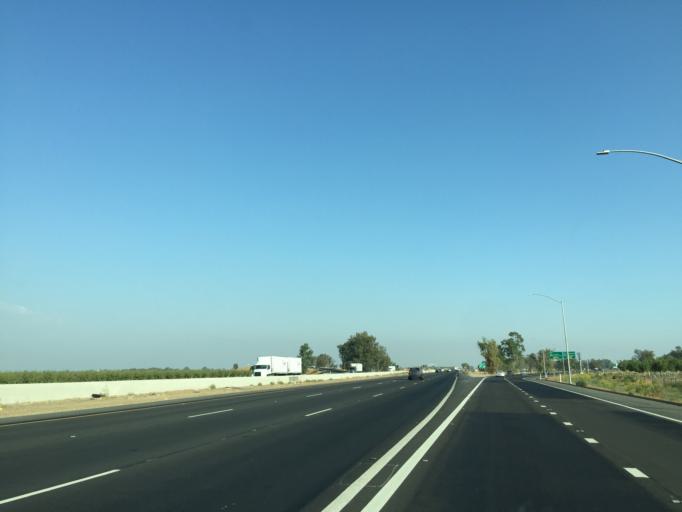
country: US
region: California
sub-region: Tulare County
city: Goshen
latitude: 36.3333
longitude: -119.4131
